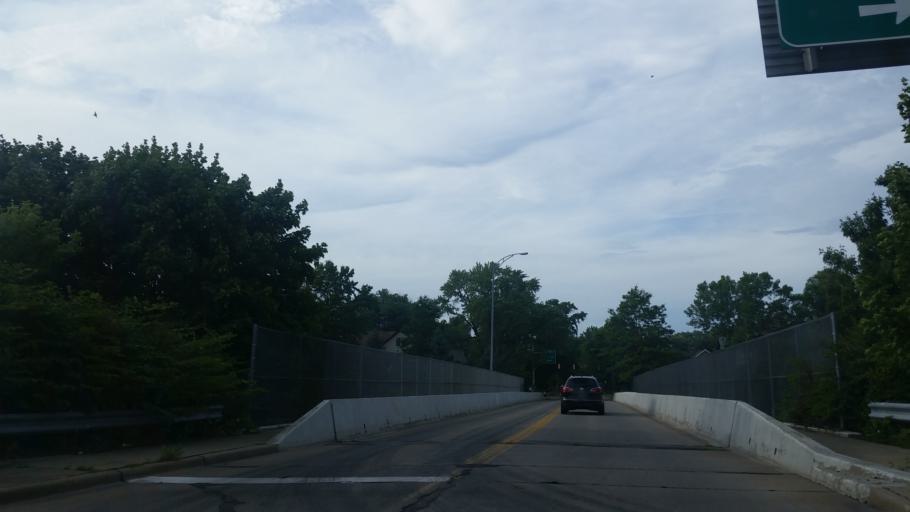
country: US
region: Ohio
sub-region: Cuyahoga County
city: Lakewood
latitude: 41.4690
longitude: -81.8088
